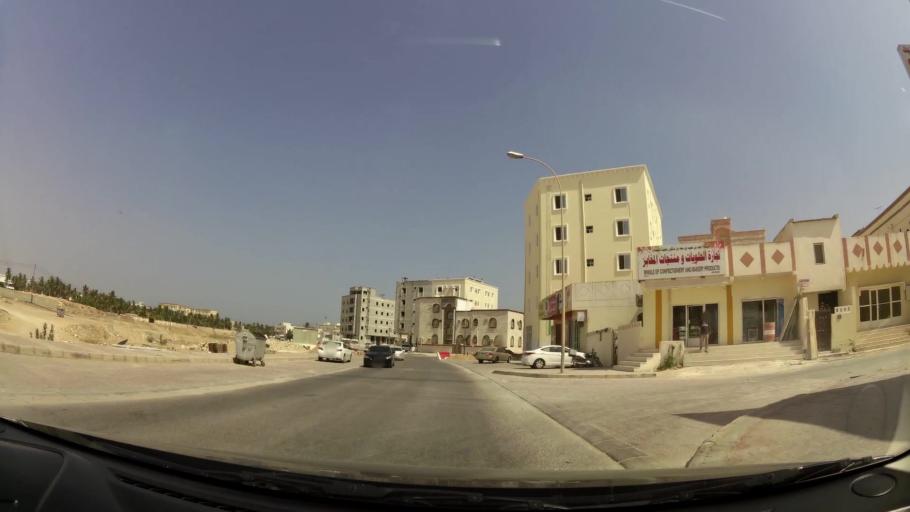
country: OM
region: Zufar
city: Salalah
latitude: 17.0149
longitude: 54.0601
